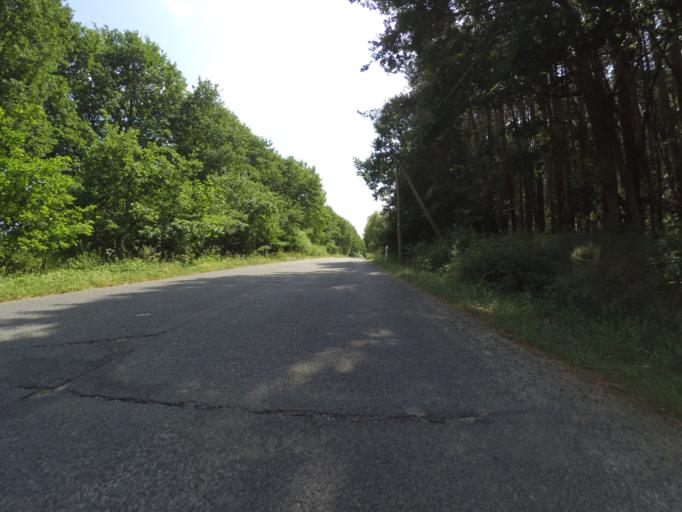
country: DE
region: Mecklenburg-Vorpommern
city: Plau am See
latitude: 53.4193
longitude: 12.3258
